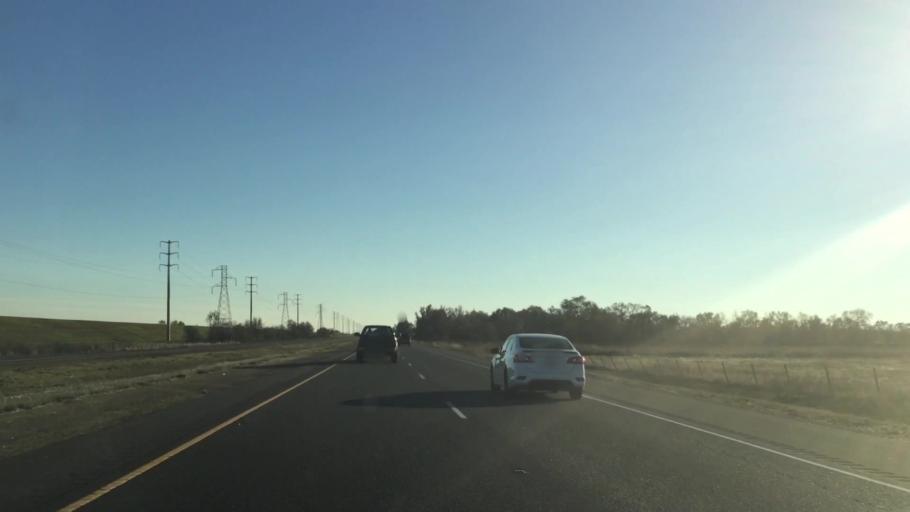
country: US
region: California
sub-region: Yuba County
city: Plumas Lake
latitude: 39.0504
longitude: -121.5434
